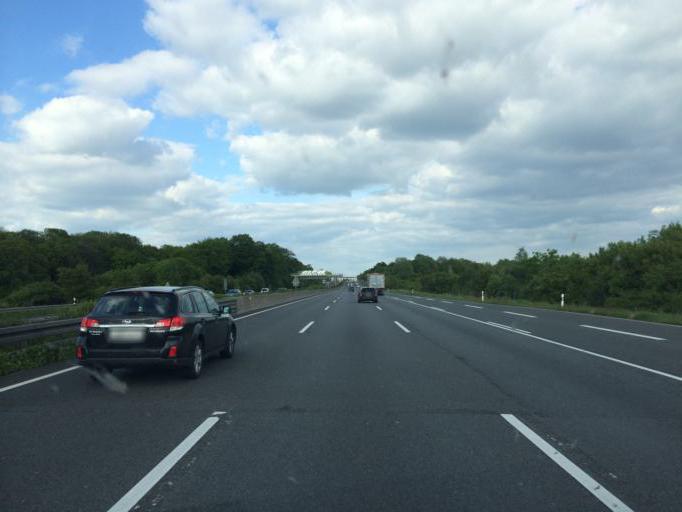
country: DE
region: Lower Saxony
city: Lehre
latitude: 52.3098
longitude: 10.7407
